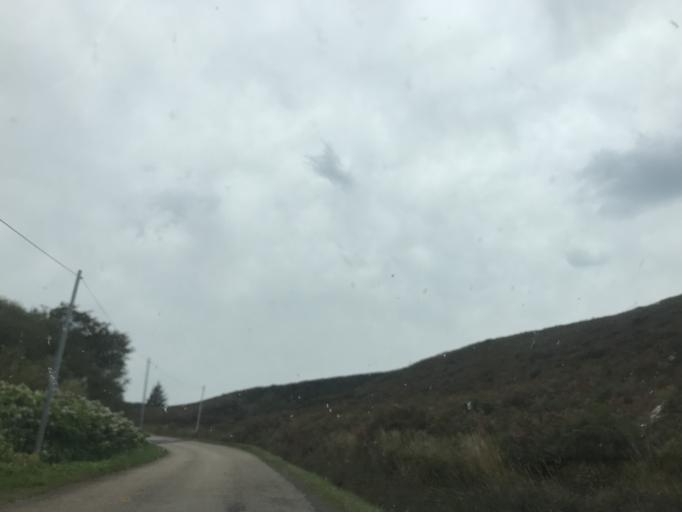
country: FR
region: Brittany
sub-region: Departement du Finistere
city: Brasparts
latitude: 48.3831
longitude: -3.9399
